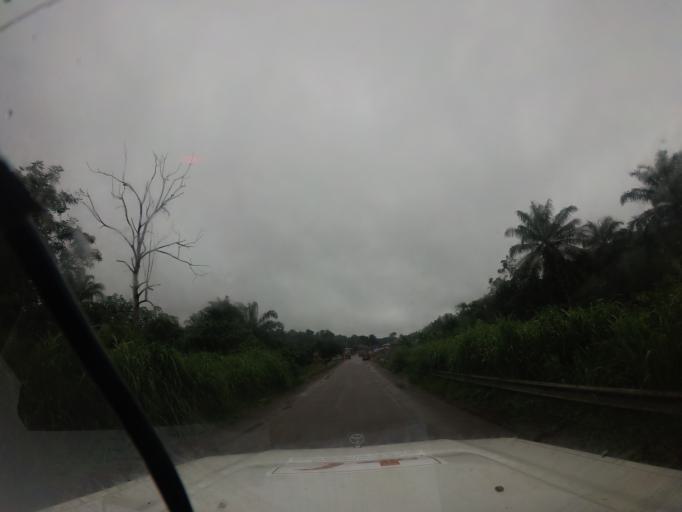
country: SL
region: Northern Province
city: Kabala
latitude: 9.5221
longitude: -11.5805
